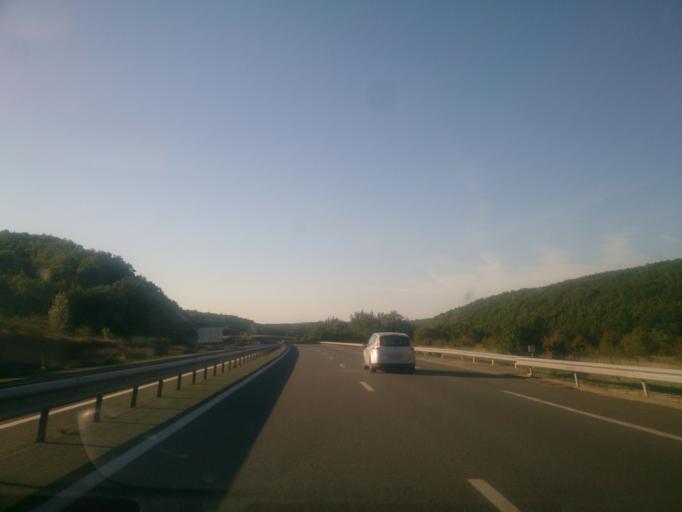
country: FR
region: Midi-Pyrenees
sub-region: Departement du Lot
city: Le Vigan
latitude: 44.7744
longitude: 1.5369
